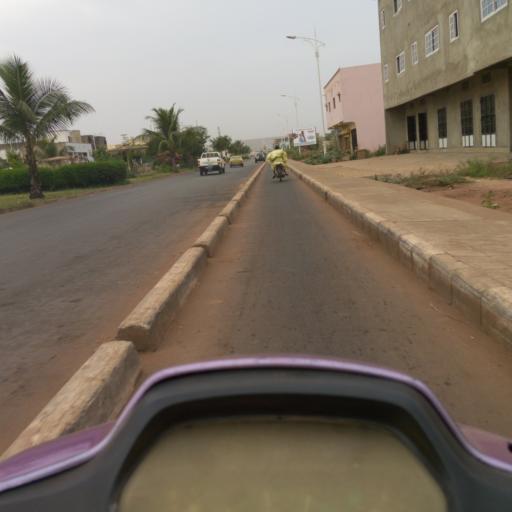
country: ML
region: Bamako
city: Bamako
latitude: 12.6540
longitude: -7.9317
